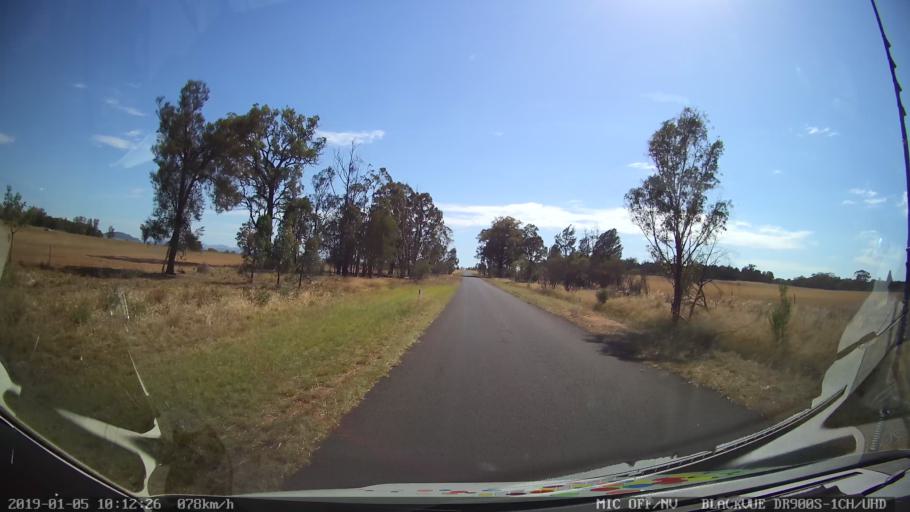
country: AU
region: New South Wales
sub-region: Gilgandra
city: Gilgandra
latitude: -31.6079
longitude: 148.9129
